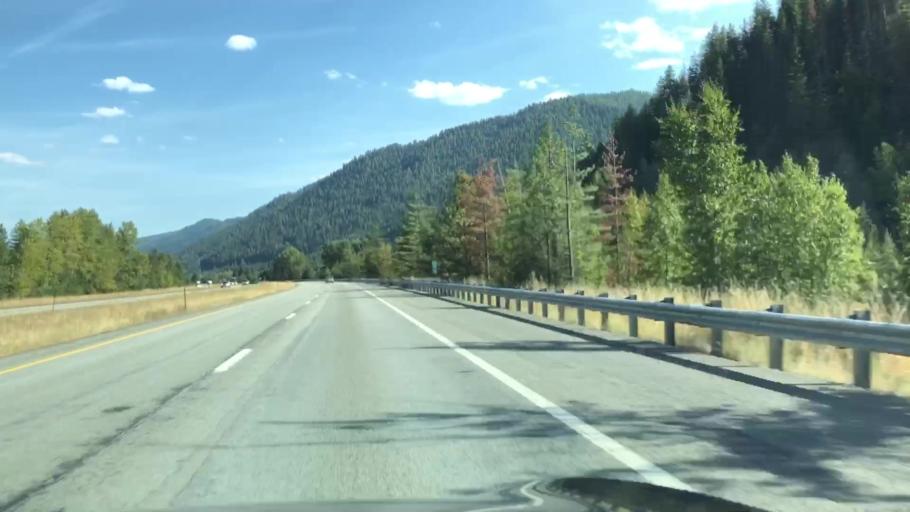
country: US
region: Idaho
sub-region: Shoshone County
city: Osburn
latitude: 47.5191
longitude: -116.0378
